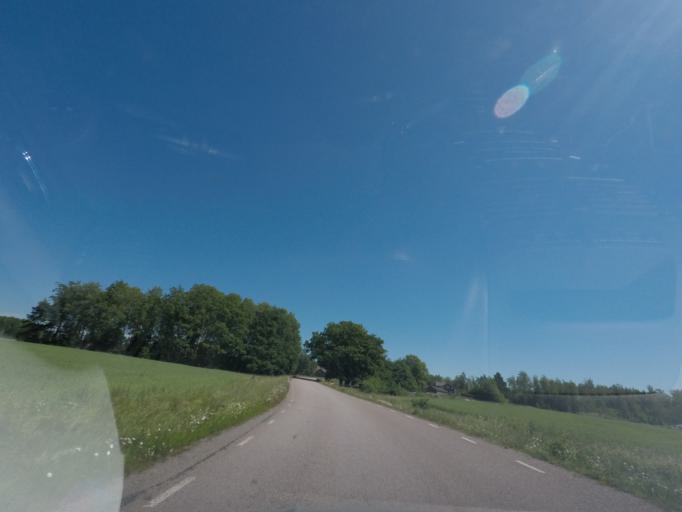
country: SE
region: Uppsala
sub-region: Enkopings Kommun
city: Irsta
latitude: 59.6812
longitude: 16.7841
